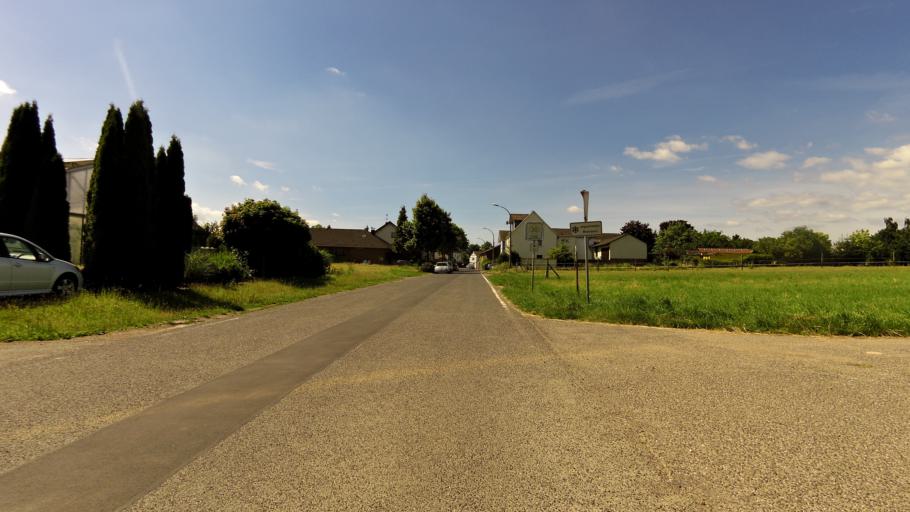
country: DE
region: North Rhine-Westphalia
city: Meckenheim
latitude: 50.6096
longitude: 6.9913
